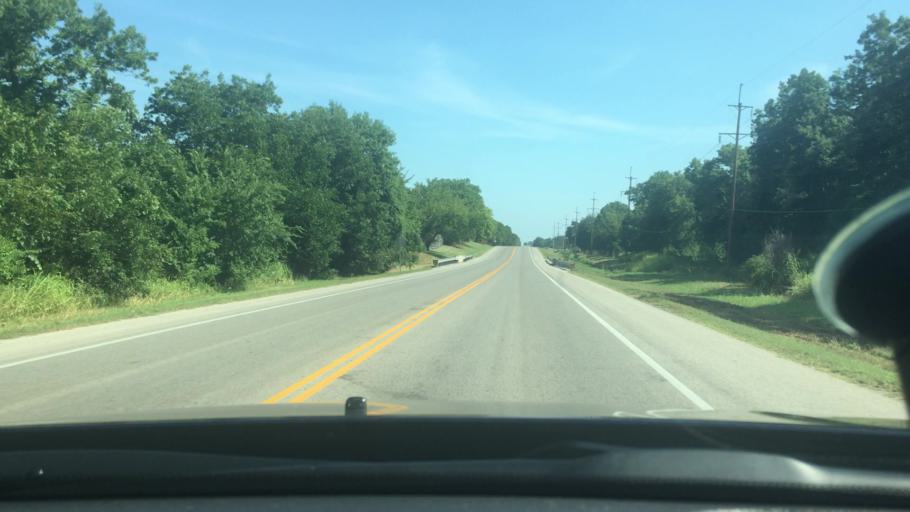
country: US
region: Oklahoma
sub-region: Garvin County
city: Pauls Valley
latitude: 34.6868
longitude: -97.2129
